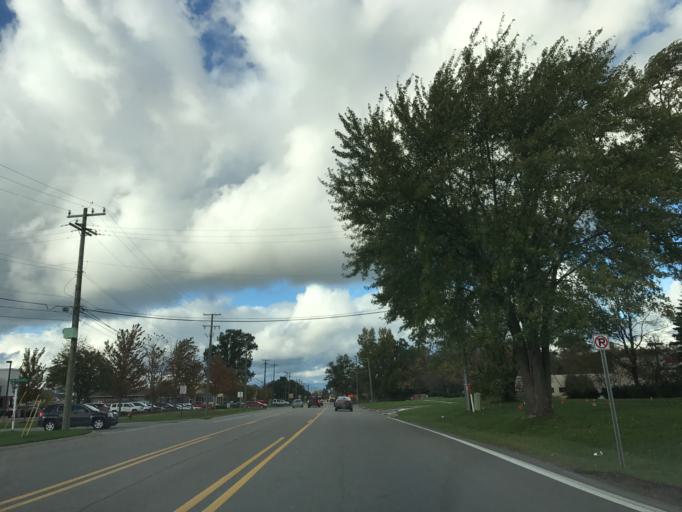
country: US
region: Michigan
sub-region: Oakland County
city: South Lyon
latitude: 42.4409
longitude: -83.6499
